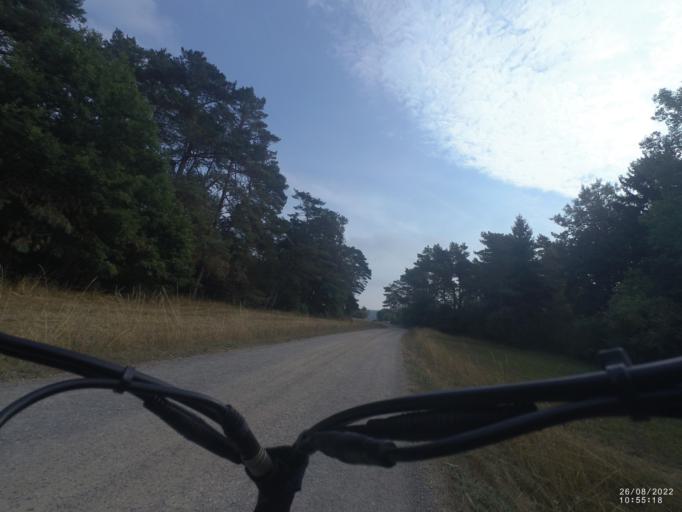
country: DE
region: Rheinland-Pfalz
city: Birresborn
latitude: 50.2013
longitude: 6.6119
